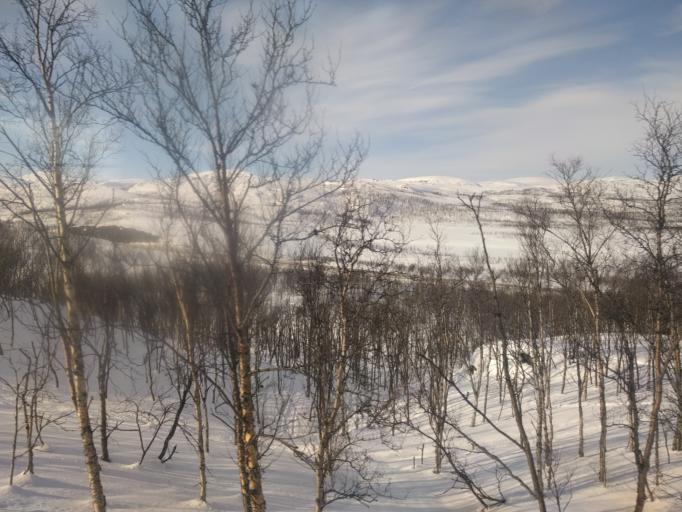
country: NO
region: Troms
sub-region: Bardu
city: Setermoen
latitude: 68.4276
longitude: 18.4701
